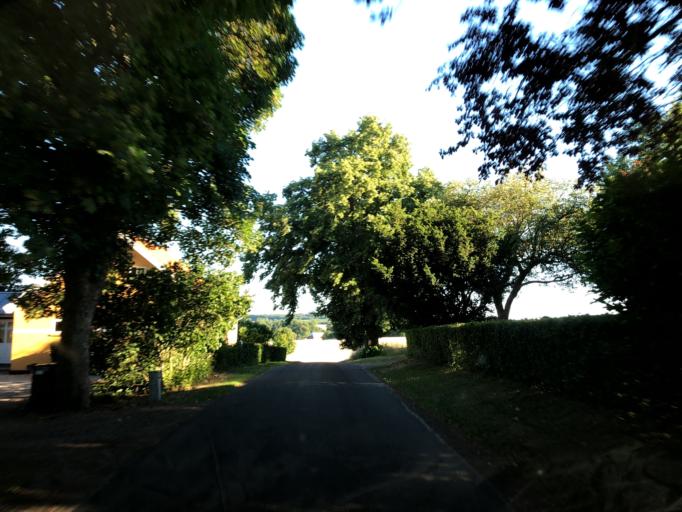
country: DK
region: Central Jutland
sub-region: Horsens Kommune
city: Horsens
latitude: 55.9384
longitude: 9.8660
